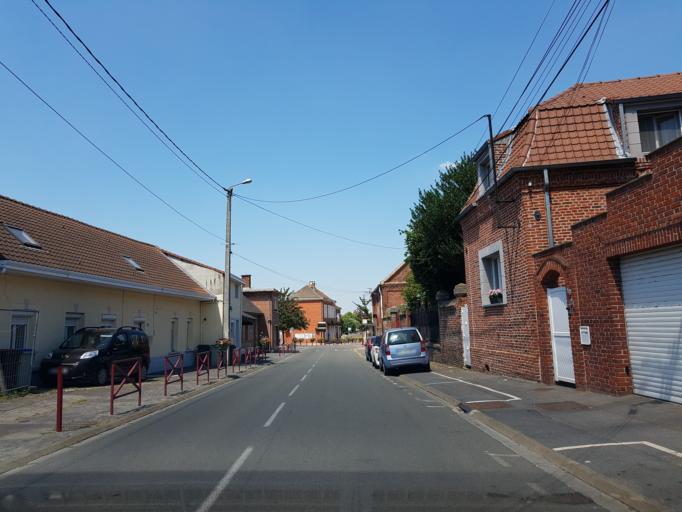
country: FR
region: Nord-Pas-de-Calais
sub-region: Departement du Nord
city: Neuville-sur-Escaut
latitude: 50.2996
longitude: 3.3539
